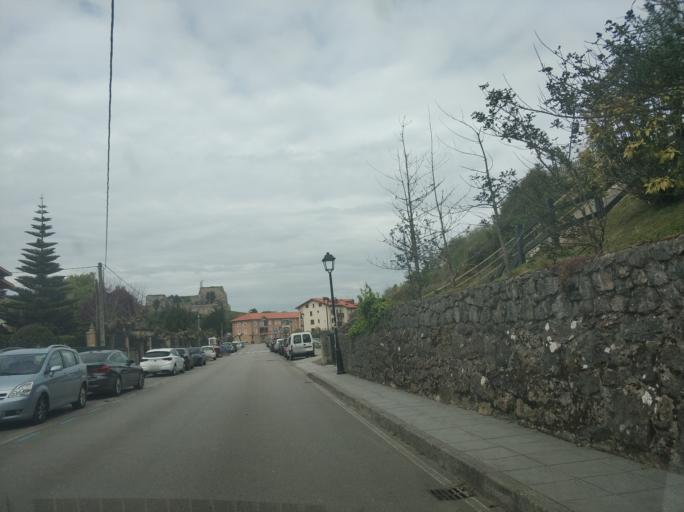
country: ES
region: Cantabria
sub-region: Provincia de Cantabria
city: Comillas
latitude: 43.3877
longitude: -4.2927
